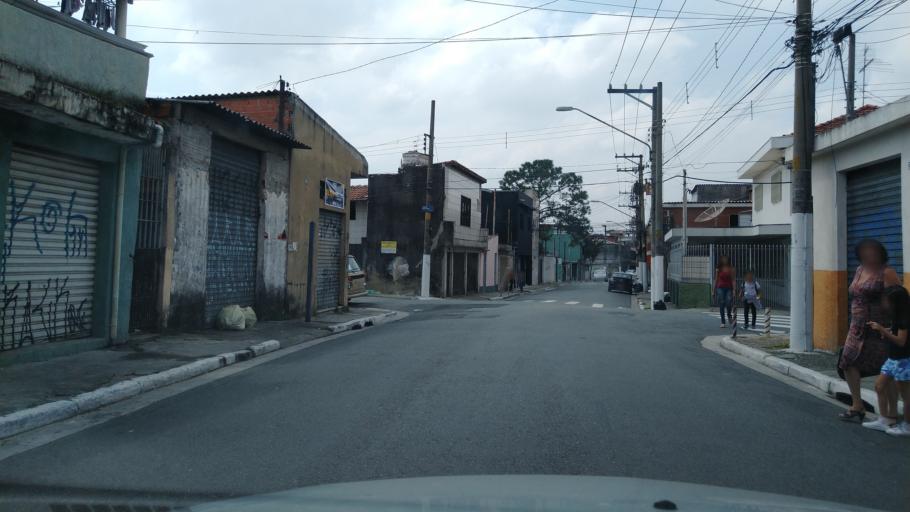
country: BR
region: Sao Paulo
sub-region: Guarulhos
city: Guarulhos
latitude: -23.4760
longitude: -46.5809
